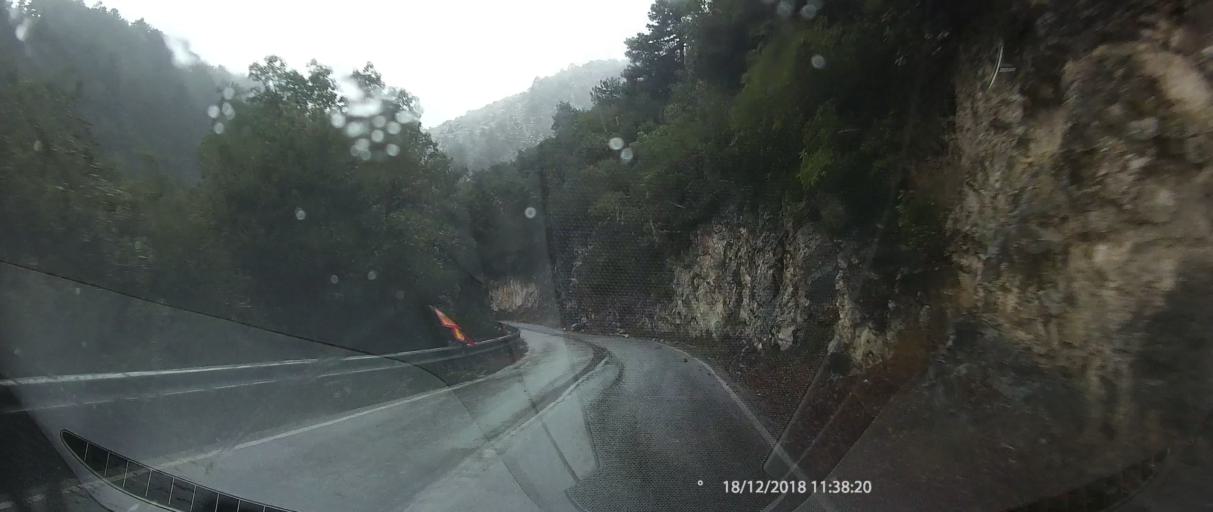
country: GR
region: Central Macedonia
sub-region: Nomos Pierias
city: Litochoro
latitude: 40.1120
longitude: 22.4789
